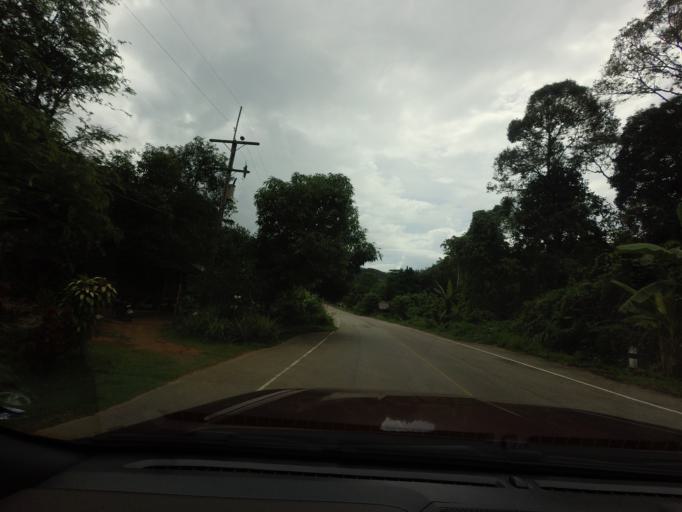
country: TH
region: Narathiwat
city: Sukhirin
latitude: 5.9837
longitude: 101.6890
